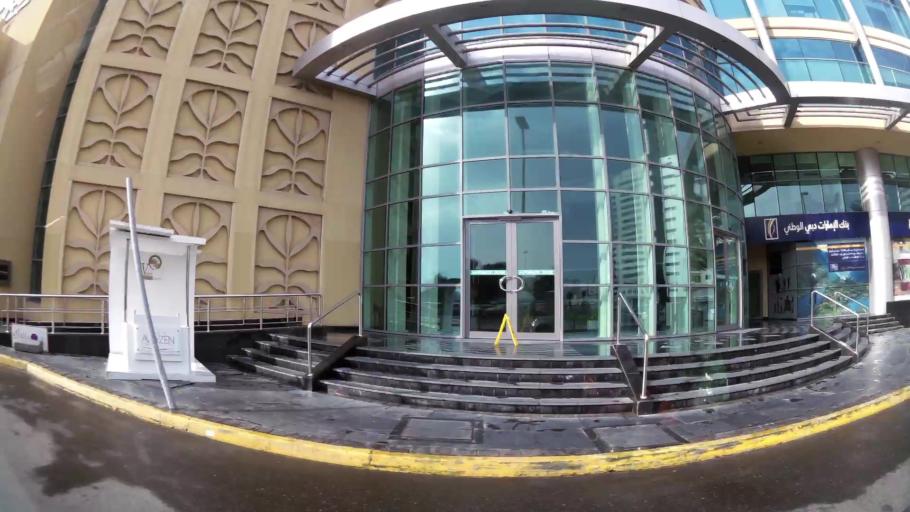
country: AE
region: Abu Dhabi
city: Abu Dhabi
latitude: 24.4720
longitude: 54.3743
